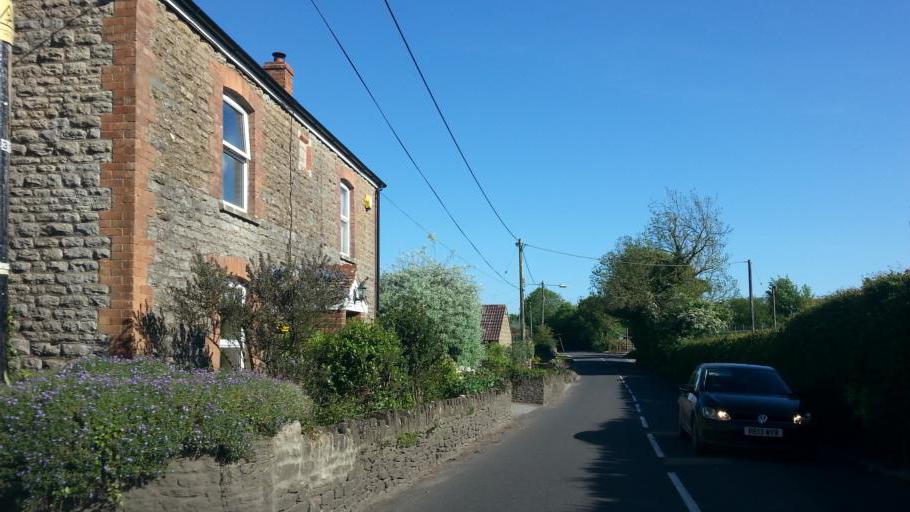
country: GB
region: England
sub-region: Dorset
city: Stalbridge
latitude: 50.9730
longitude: -2.3904
